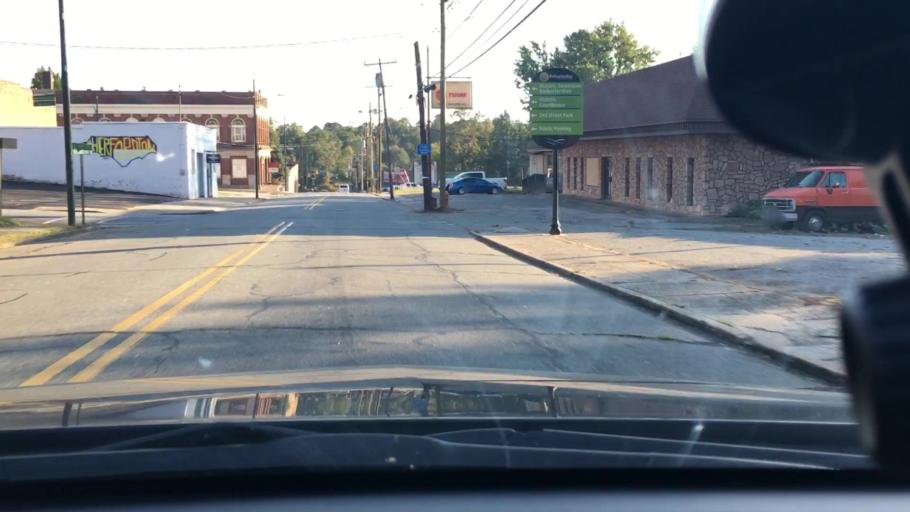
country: US
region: North Carolina
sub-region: Rutherford County
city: Rutherfordton
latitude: 35.3692
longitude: -81.9585
